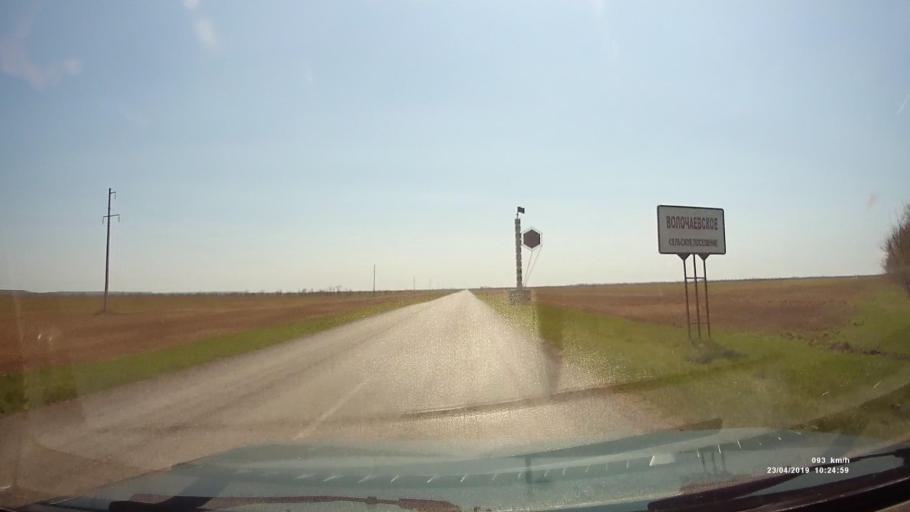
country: RU
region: Rostov
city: Sovetskoye
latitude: 46.6345
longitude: 42.4499
